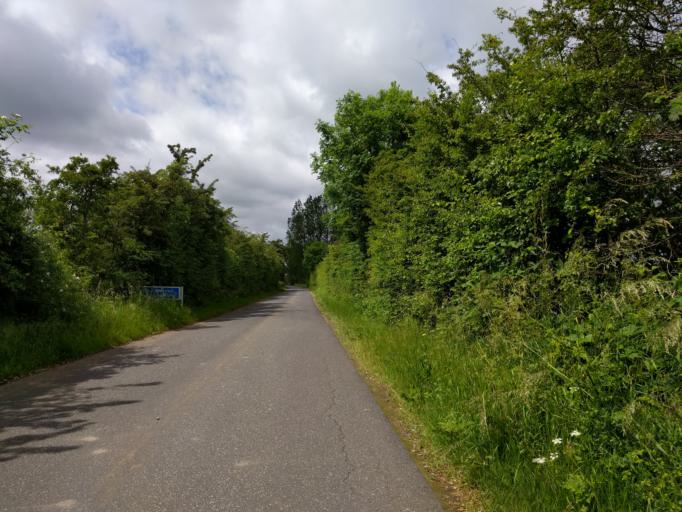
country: DK
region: South Denmark
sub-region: Odense Kommune
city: Bullerup
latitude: 55.4202
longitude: 10.5199
